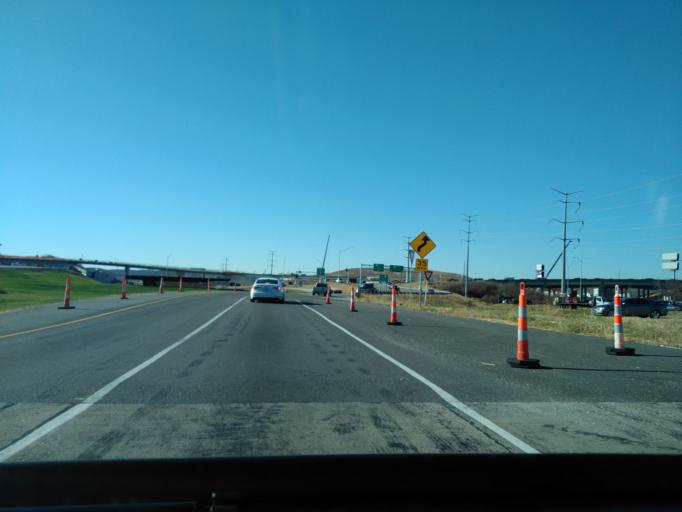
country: US
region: Missouri
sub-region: Saint Louis County
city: Valley Park
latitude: 38.5404
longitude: -90.4925
